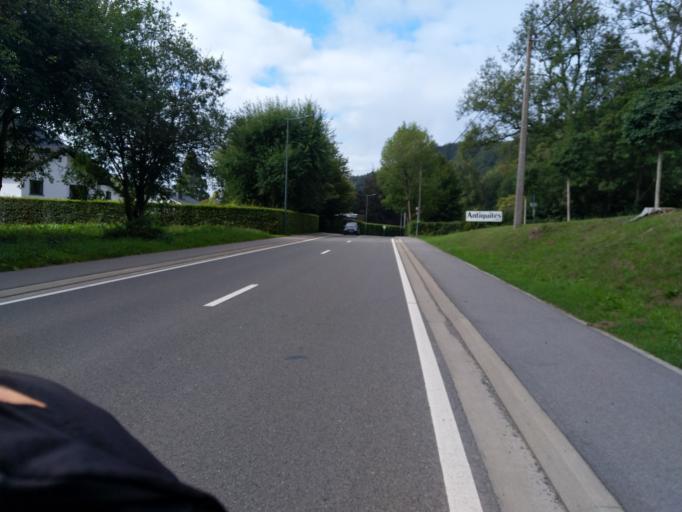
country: BE
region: Wallonia
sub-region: Province de Liege
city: Malmedy
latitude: 50.4401
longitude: 6.0329
